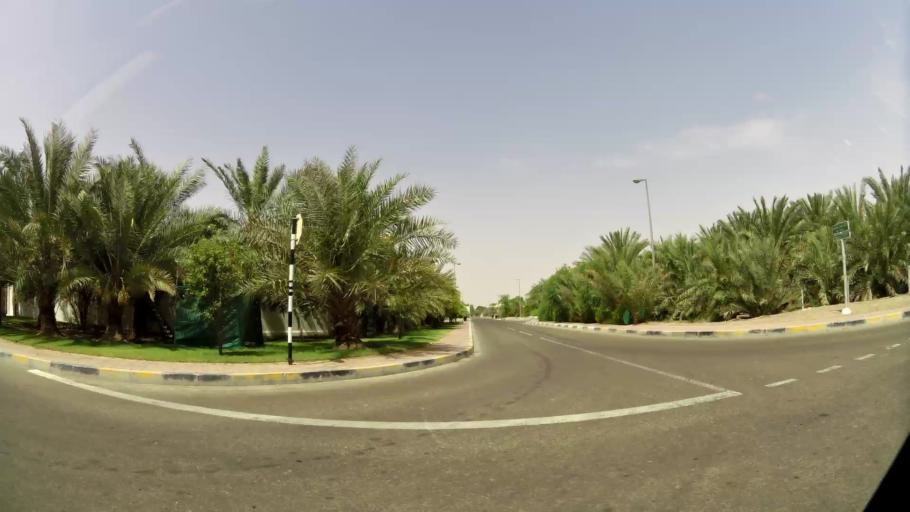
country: AE
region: Abu Dhabi
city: Al Ain
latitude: 24.1804
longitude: 55.7163
